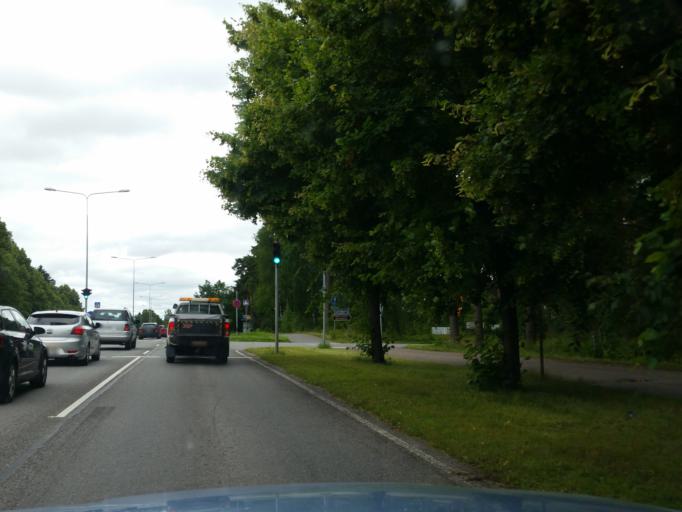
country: FI
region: Varsinais-Suomi
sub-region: Turku
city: Turku
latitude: 60.4320
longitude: 22.3005
